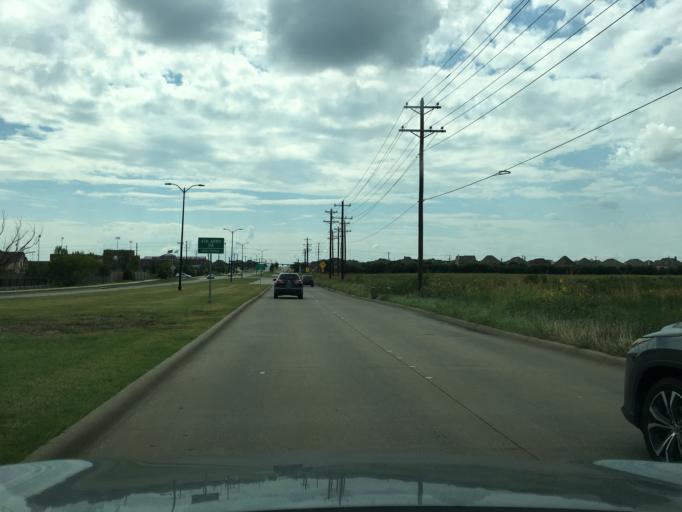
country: US
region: Texas
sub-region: Collin County
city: Frisco
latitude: 33.1331
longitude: -96.8567
